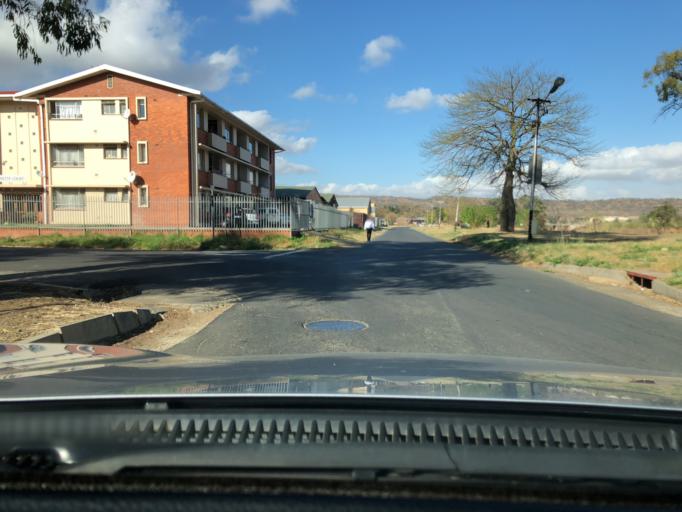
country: ZA
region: KwaZulu-Natal
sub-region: uThukela District Municipality
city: Ladysmith
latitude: -28.5633
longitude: 29.7765
